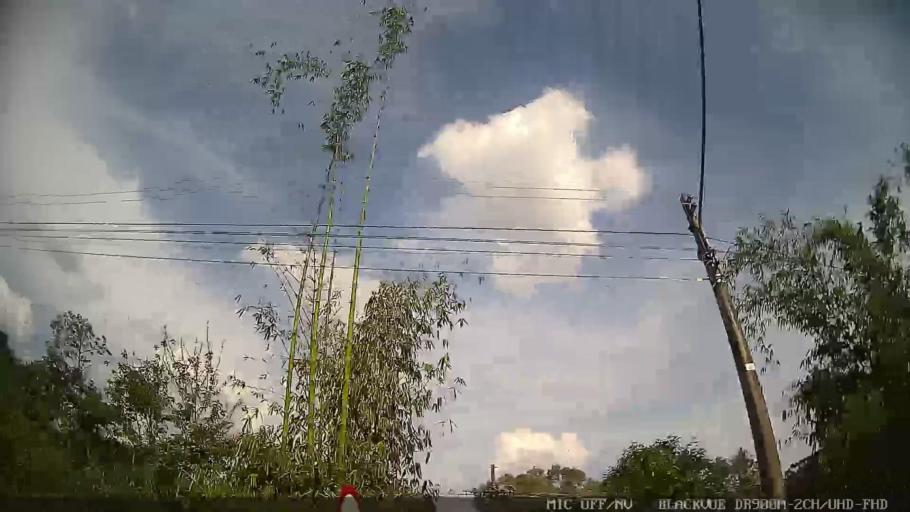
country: BR
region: Sao Paulo
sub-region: Braganca Paulista
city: Braganca Paulista
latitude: -22.9040
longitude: -46.5436
